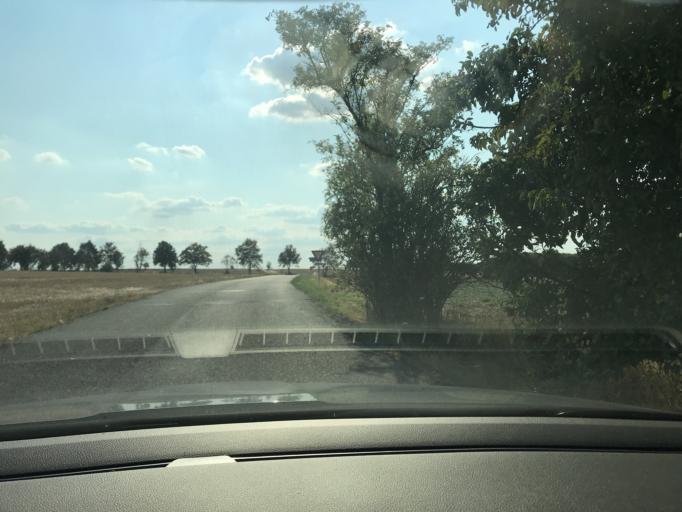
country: CZ
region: Central Bohemia
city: Kralupy nad Vltavou
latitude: 50.2156
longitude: 14.3194
